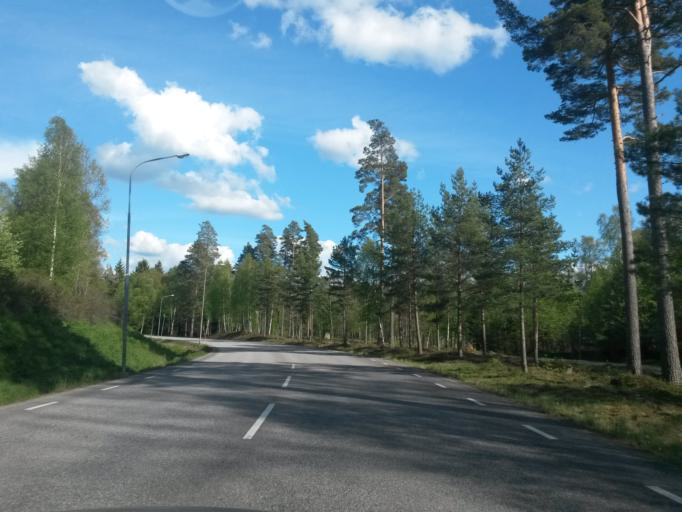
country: SE
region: Vaestra Goetaland
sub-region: Herrljunga Kommun
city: Herrljunga
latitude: 58.0723
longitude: 13.0342
